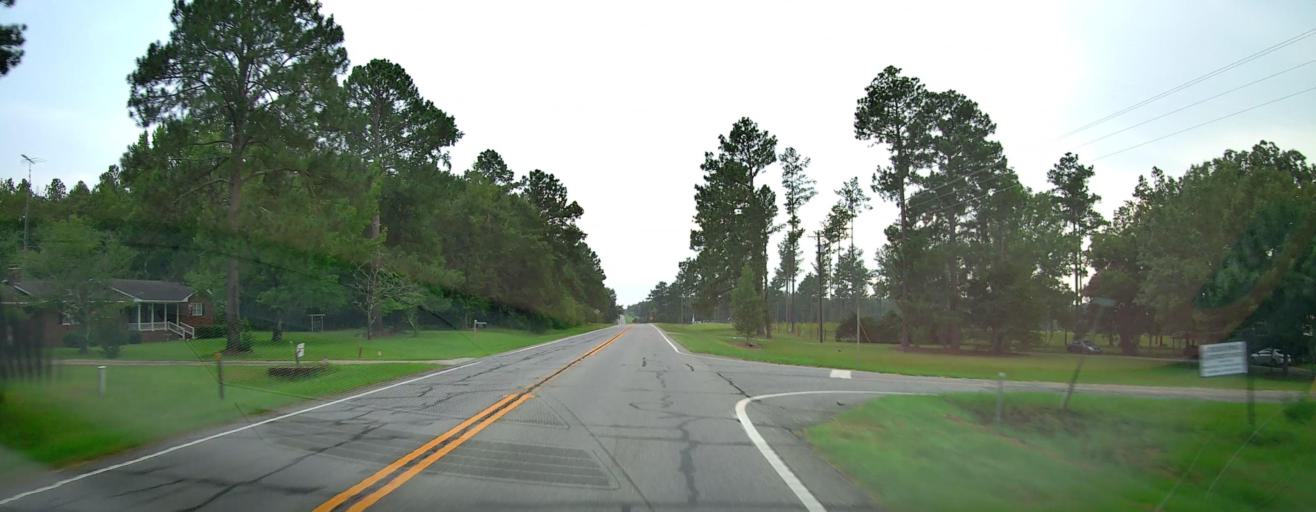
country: US
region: Georgia
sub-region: Laurens County
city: East Dublin
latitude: 32.6345
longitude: -82.8063
